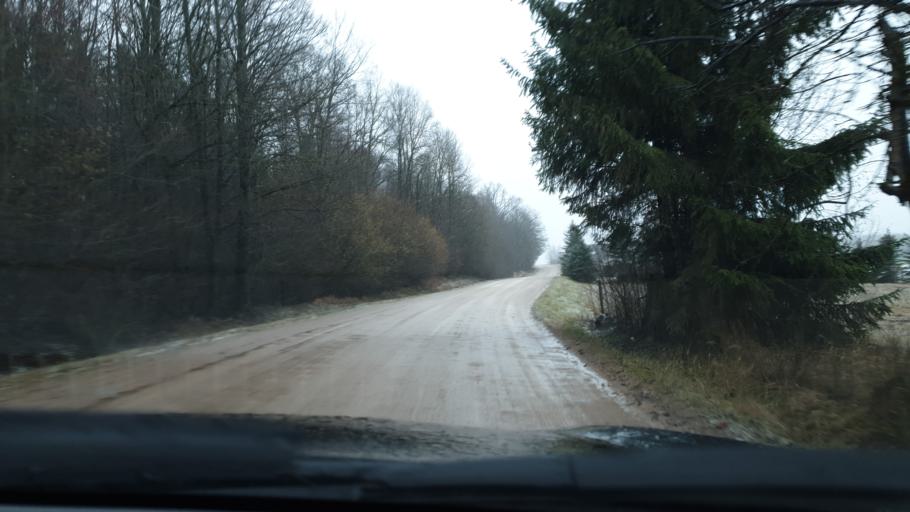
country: LT
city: Jieznas
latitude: 54.5679
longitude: 24.3186
